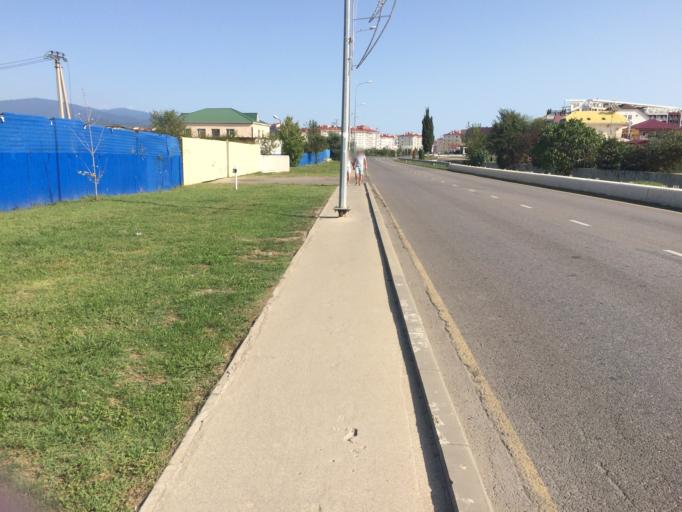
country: RU
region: Krasnodarskiy
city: Adler
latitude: 43.3938
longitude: 39.9860
